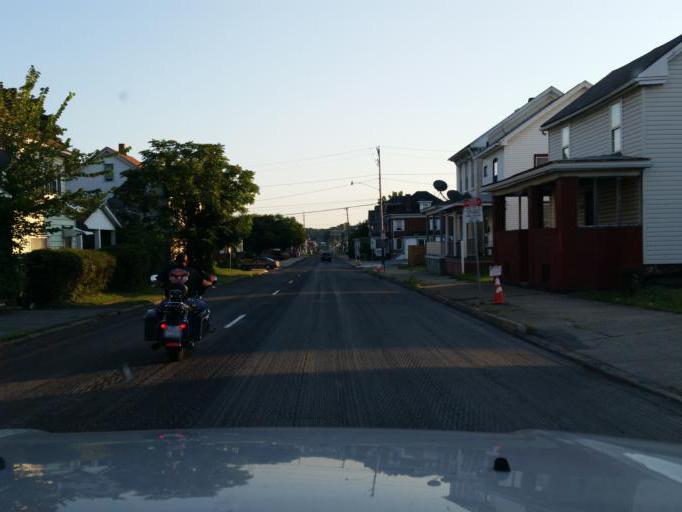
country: US
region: Pennsylvania
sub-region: Blair County
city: Altoona
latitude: 40.5077
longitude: -78.4018
